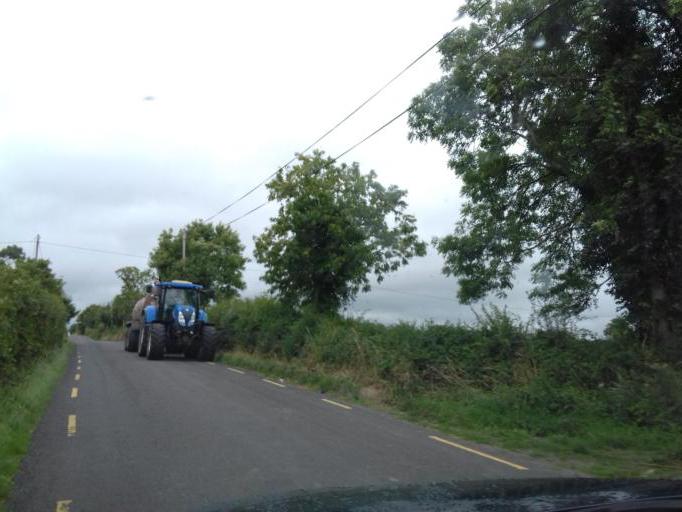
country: IE
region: Leinster
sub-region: Kilkenny
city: Graiguenamanagh
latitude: 52.6166
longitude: -7.0356
